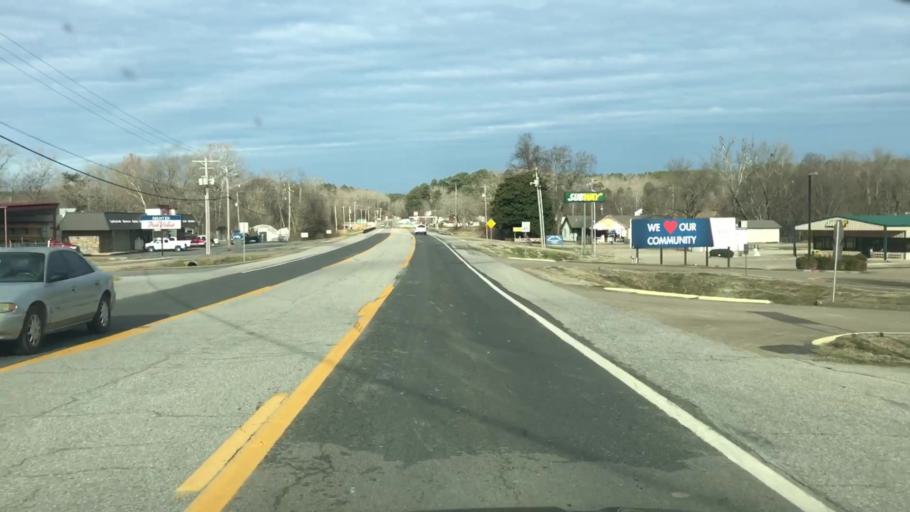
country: US
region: Arkansas
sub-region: Montgomery County
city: Mount Ida
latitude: 34.5591
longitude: -93.6340
